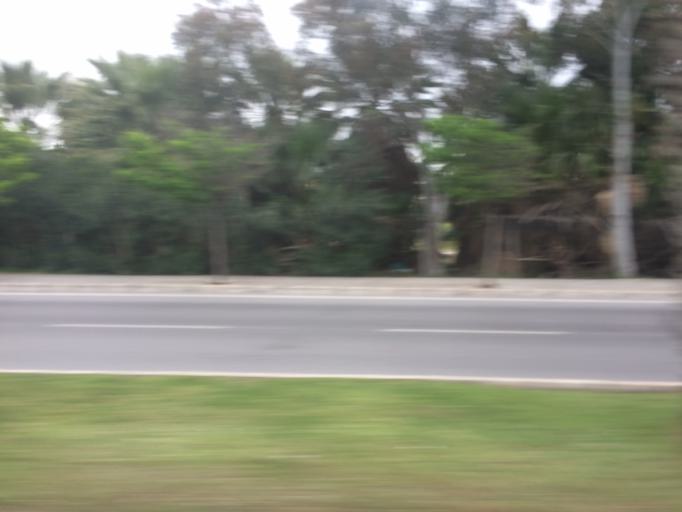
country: TR
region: Izmir
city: Izmir
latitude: 38.4543
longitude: 27.1683
